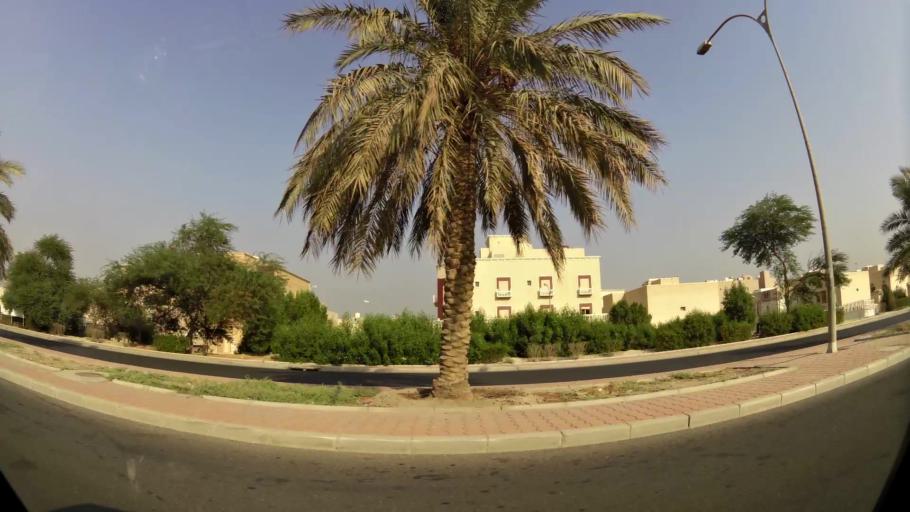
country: KW
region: Al Ahmadi
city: Ar Riqqah
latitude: 29.1320
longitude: 48.1032
